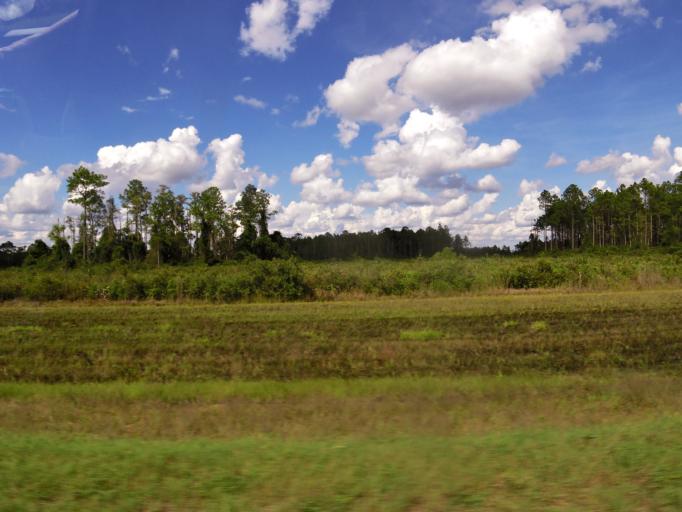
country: US
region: Georgia
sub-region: Echols County
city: Statenville
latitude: 30.6940
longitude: -82.8994
